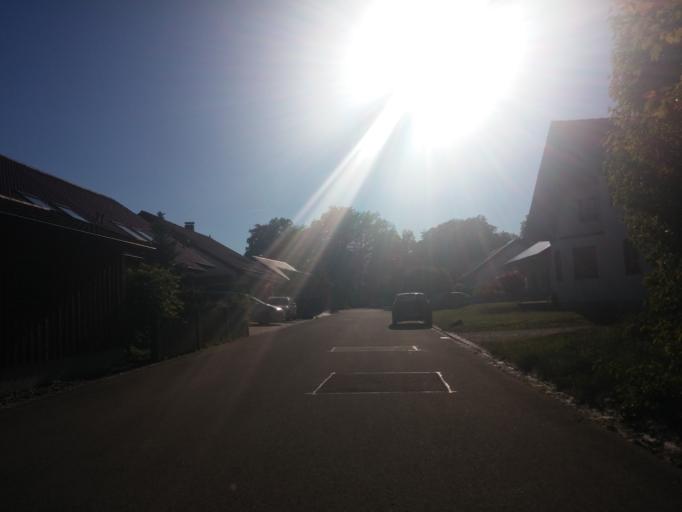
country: DE
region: Bavaria
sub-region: Swabia
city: Lautrach
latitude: 47.8959
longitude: 10.1184
